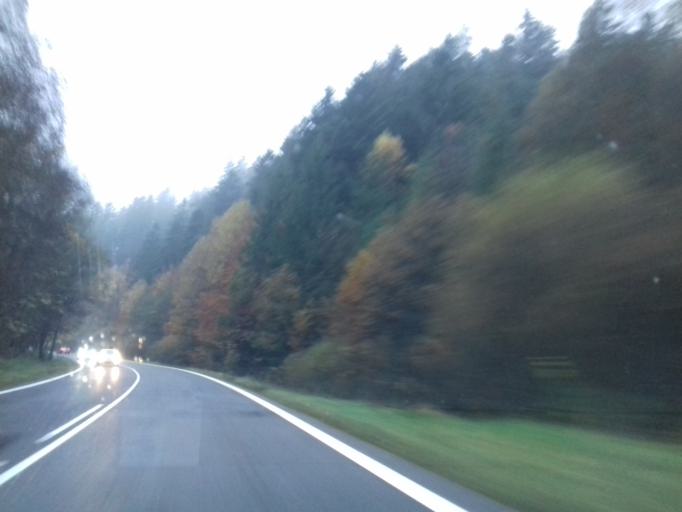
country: SK
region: Banskobystricky
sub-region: Okres Banska Bystrica
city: Banska Bystrica
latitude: 48.8313
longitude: 19.1018
